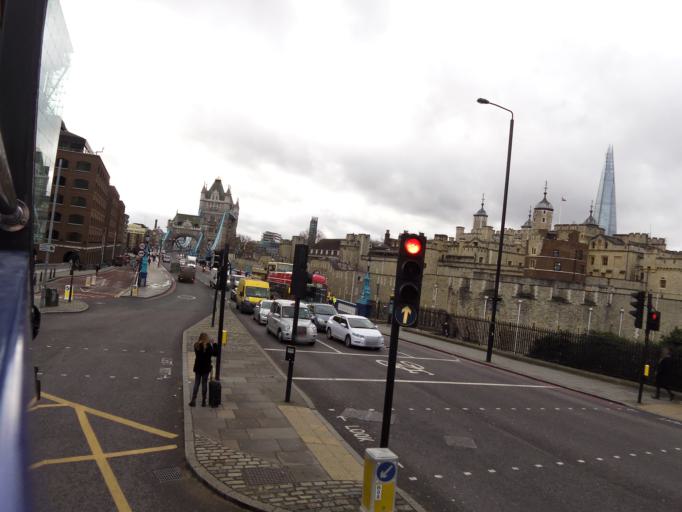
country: GB
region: England
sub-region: Greater London
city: City of London
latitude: 51.5092
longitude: -0.0737
